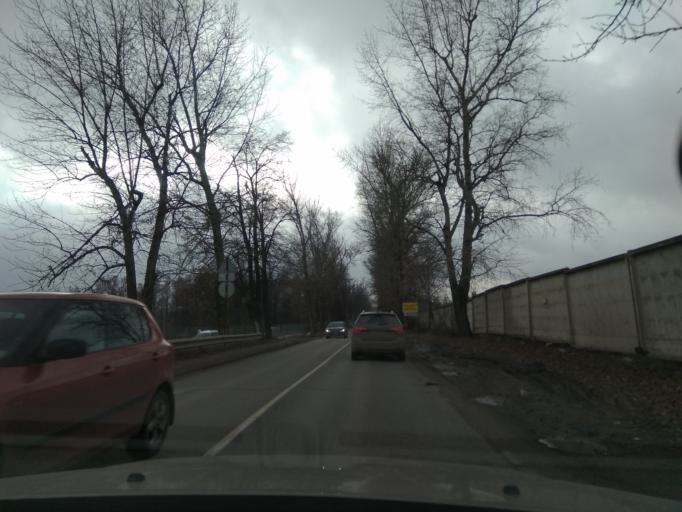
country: RU
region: Moscow
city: Zagor'ye
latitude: 55.5645
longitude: 37.6870
